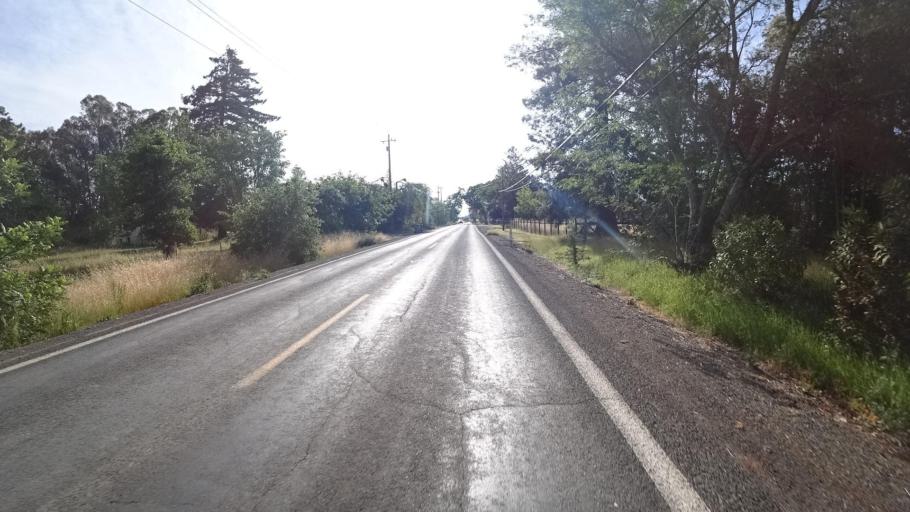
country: US
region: California
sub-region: Lake County
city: Lakeport
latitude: 39.0081
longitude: -122.8907
